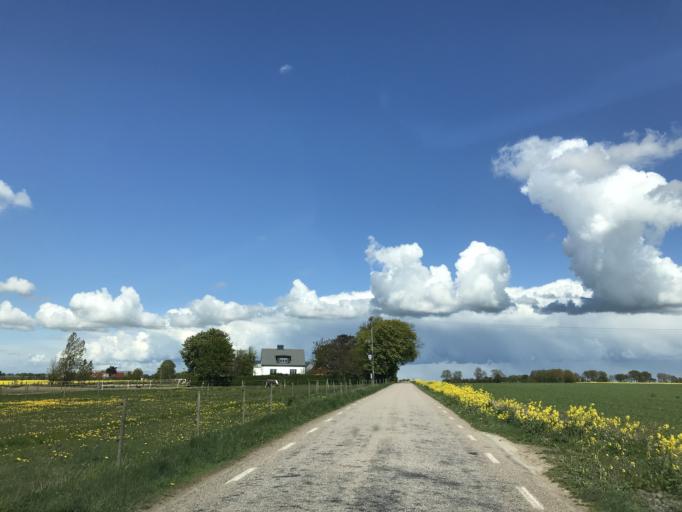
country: SE
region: Skane
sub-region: Helsingborg
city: Glumslov
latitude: 55.9664
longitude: 12.8894
